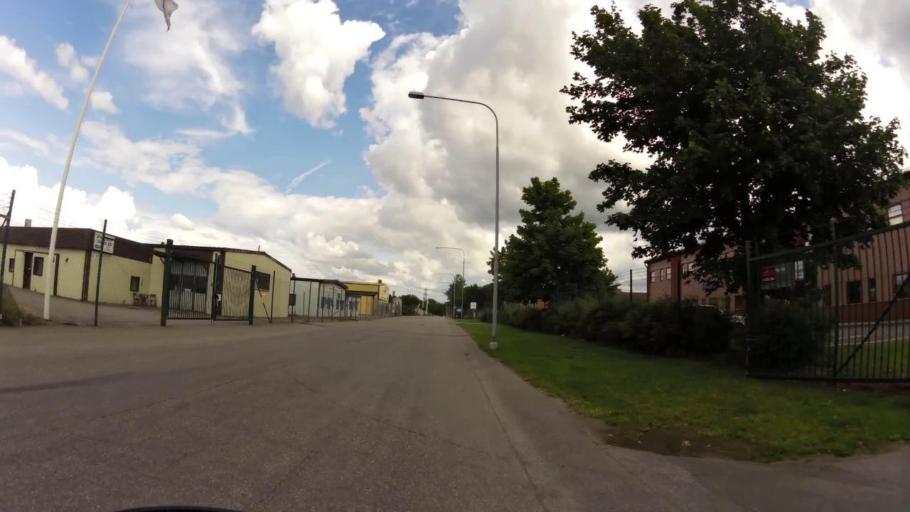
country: SE
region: OEstergoetland
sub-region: Linkopings Kommun
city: Linkoping
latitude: 58.4307
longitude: 15.6139
